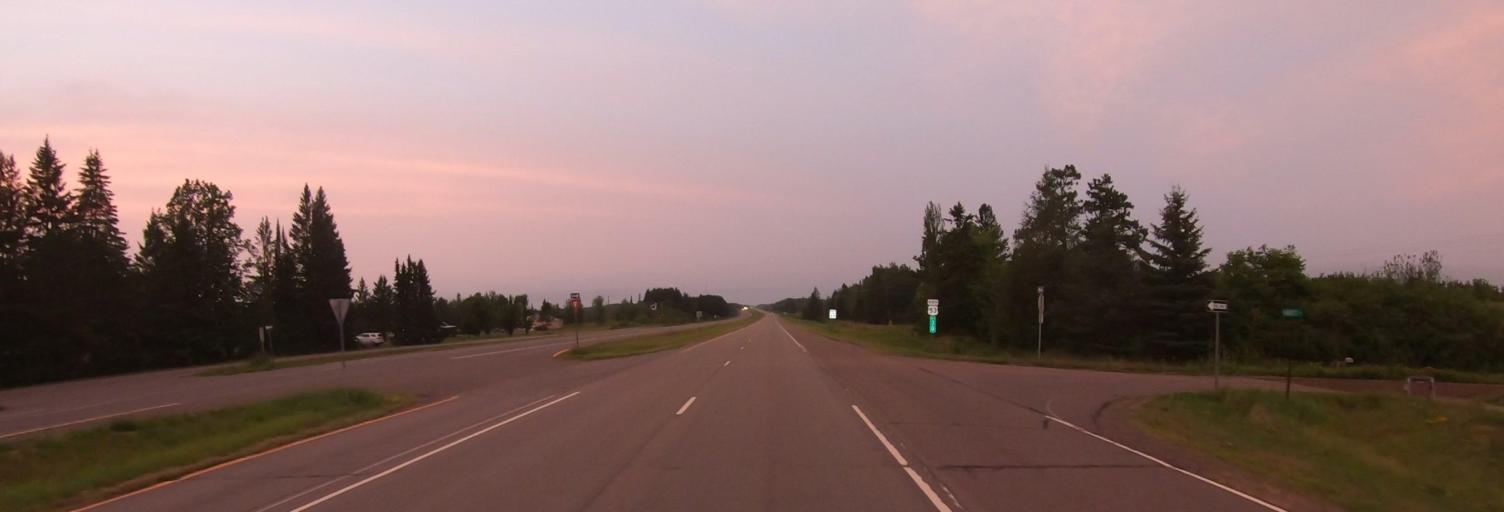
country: US
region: Minnesota
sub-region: Carlton County
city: Cloquet
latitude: 47.0394
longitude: -92.4704
